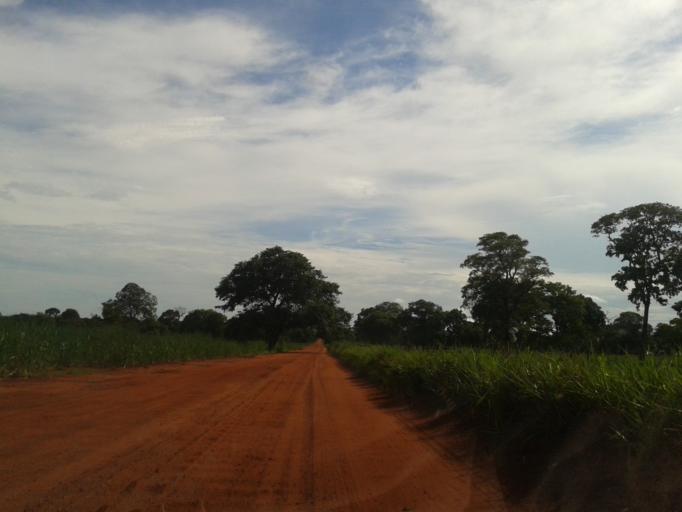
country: BR
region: Minas Gerais
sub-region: Santa Vitoria
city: Santa Vitoria
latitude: -19.1966
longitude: -50.6450
